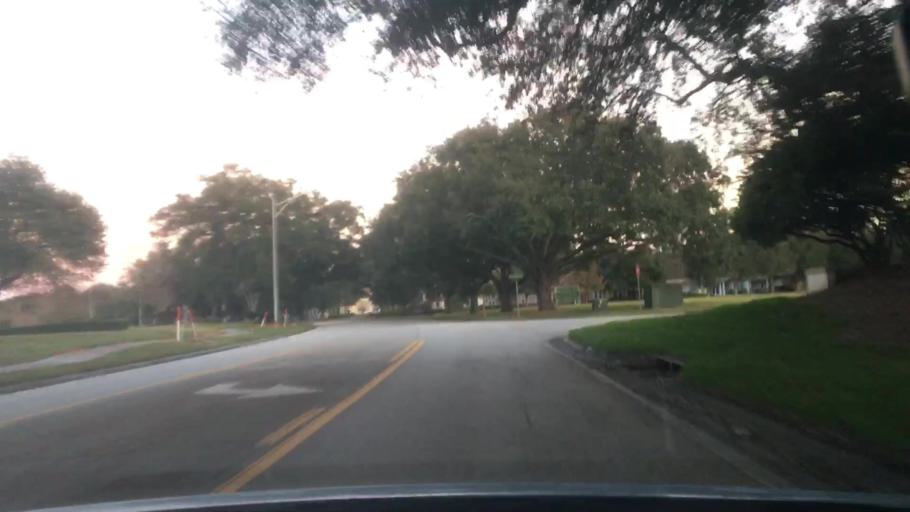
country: US
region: Florida
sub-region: Duval County
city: Jacksonville
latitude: 30.2584
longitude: -81.5915
